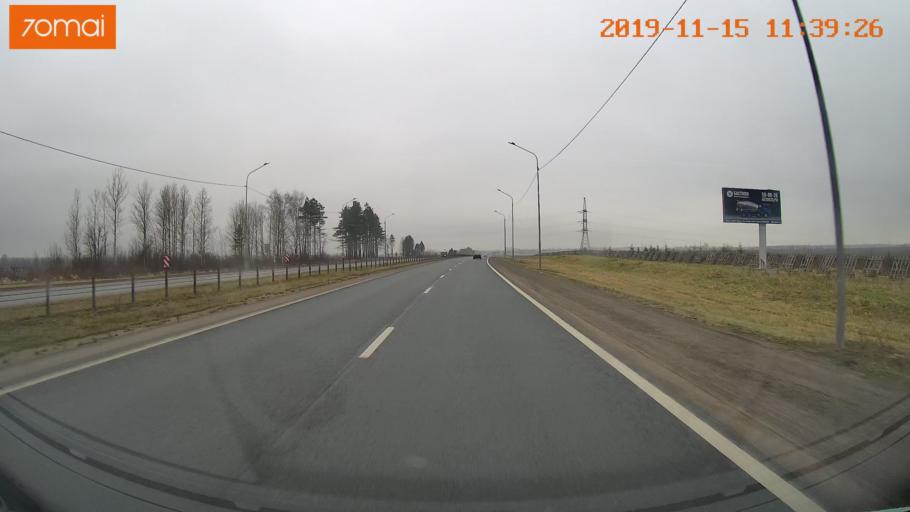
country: RU
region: Vologda
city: Molochnoye
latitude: 59.2114
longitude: 39.7242
